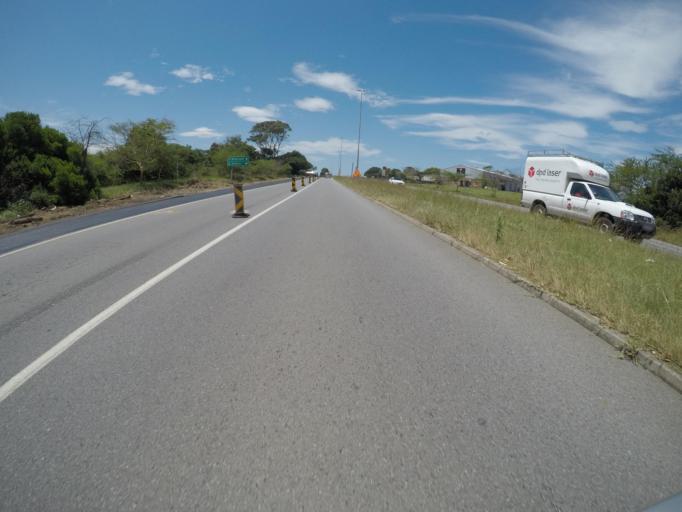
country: ZA
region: Eastern Cape
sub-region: Buffalo City Metropolitan Municipality
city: East London
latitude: -33.0356
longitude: 27.8390
